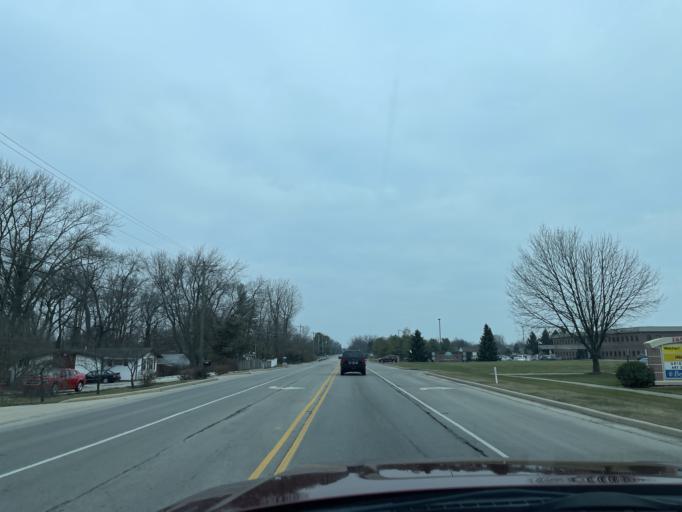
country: US
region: Indiana
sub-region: Hendricks County
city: Fairfield Heights
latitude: 39.8224
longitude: -86.4010
